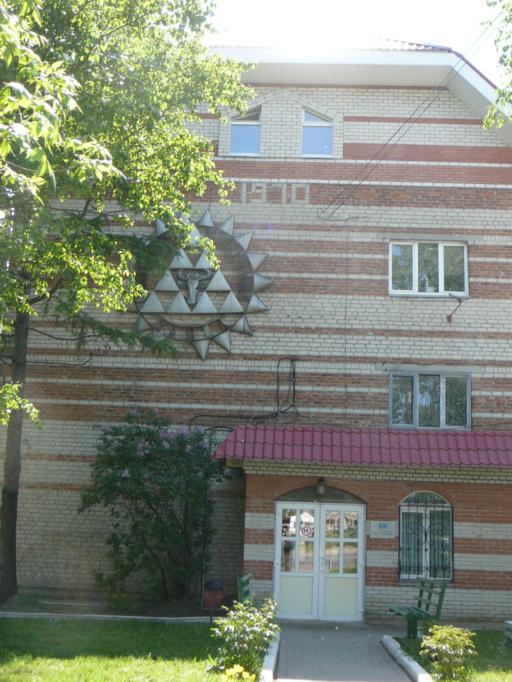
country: RU
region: Smolensk
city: Smolensk
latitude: 54.7688
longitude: 31.9969
